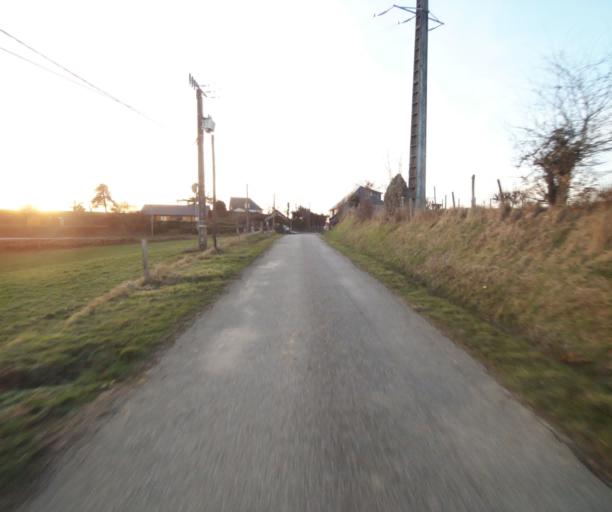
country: FR
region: Limousin
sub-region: Departement de la Correze
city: Laguenne
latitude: 45.2231
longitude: 1.8272
